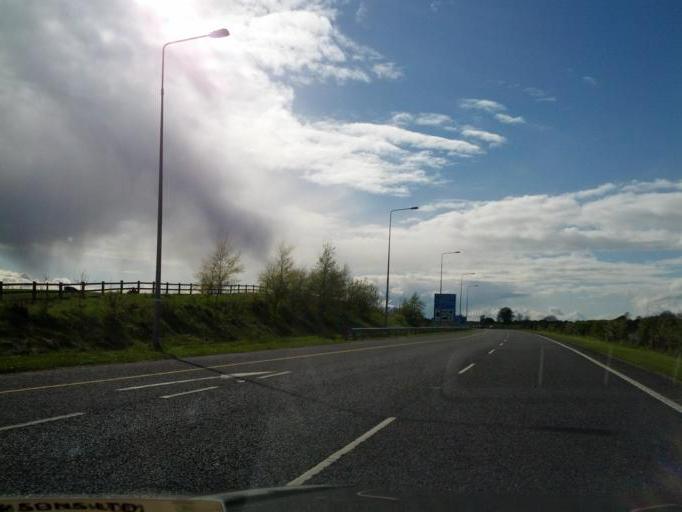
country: IE
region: Leinster
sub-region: An Mhi
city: Enfield
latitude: 53.4121
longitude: -6.8563
